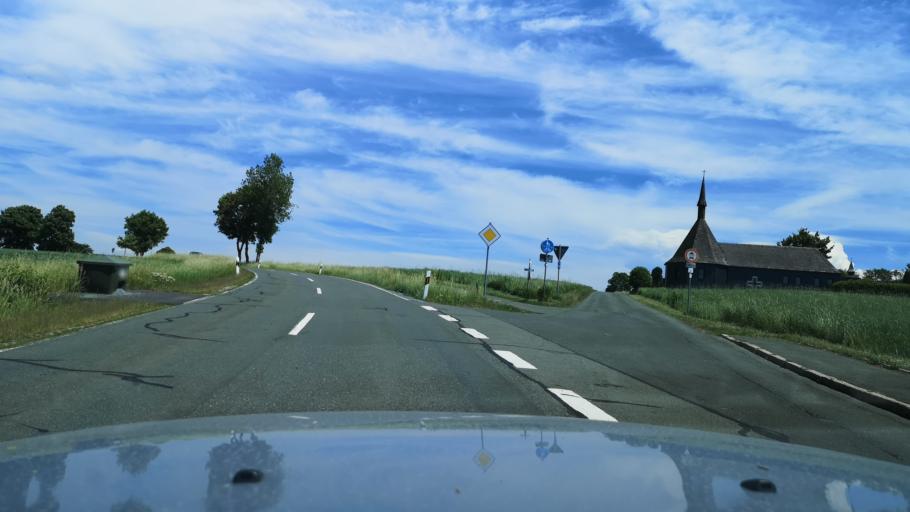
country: DE
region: Thuringia
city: Schlegel
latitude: 50.3747
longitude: 11.5992
